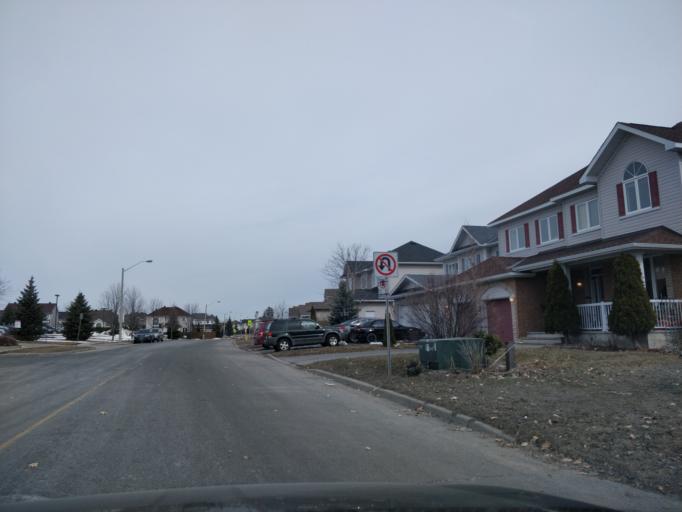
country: CA
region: Ontario
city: Bells Corners
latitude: 45.2707
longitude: -75.9072
